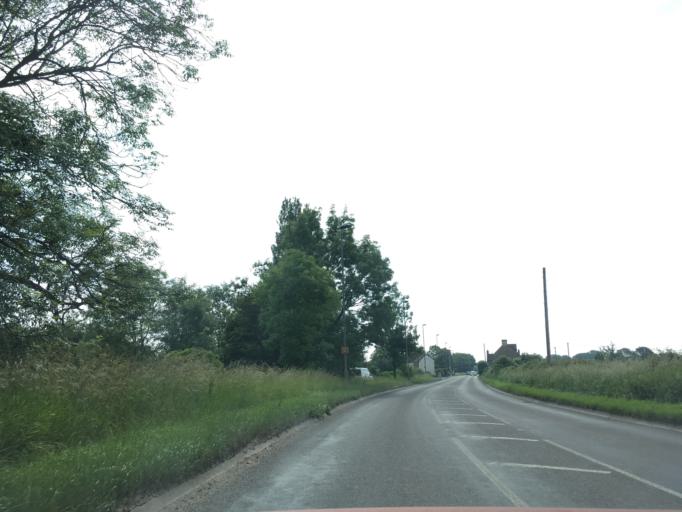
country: GB
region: England
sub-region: South Gloucestershire
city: Yate
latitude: 51.5485
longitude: -2.4531
